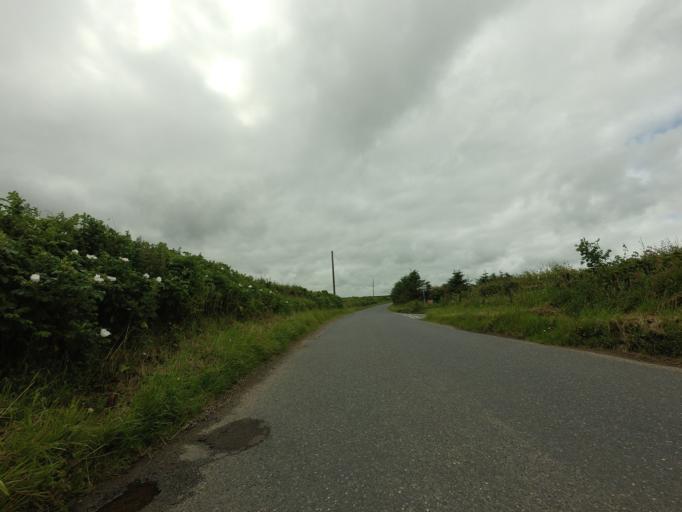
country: GB
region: Scotland
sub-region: Aberdeenshire
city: Rosehearty
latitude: 57.5401
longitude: -2.1934
